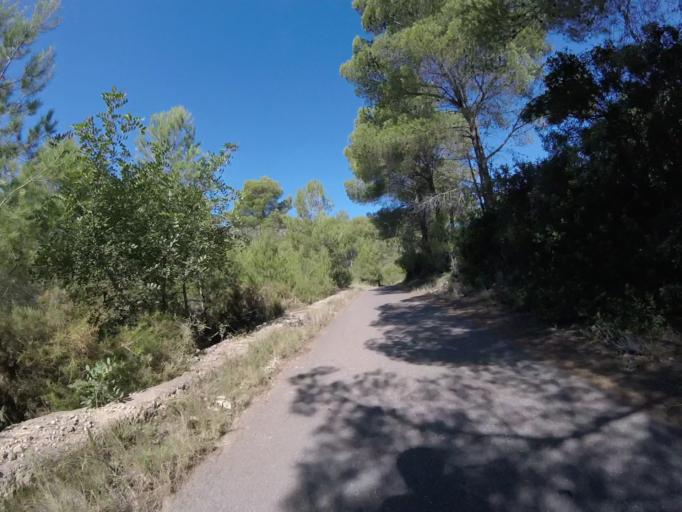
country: ES
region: Valencia
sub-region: Provincia de Castello
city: Cabanes
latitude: 40.1397
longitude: 0.1022
